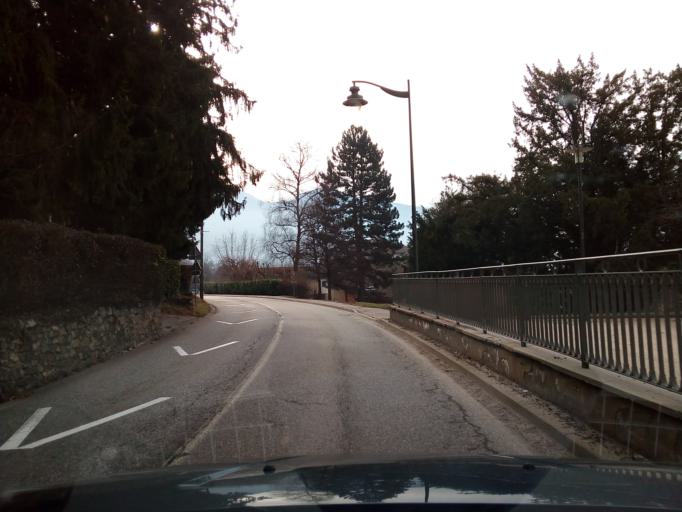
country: FR
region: Rhone-Alpes
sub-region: Departement de l'Isere
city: Vaulnaveys-le-Haut
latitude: 45.1502
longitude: 5.8366
